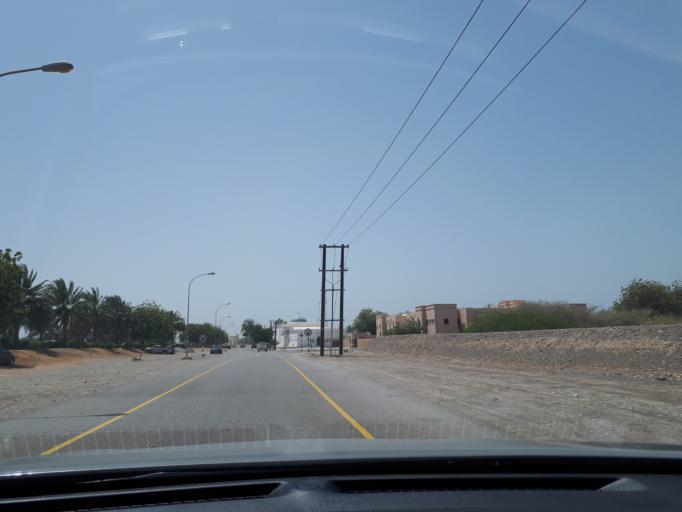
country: OM
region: Muhafazat Masqat
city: As Sib al Jadidah
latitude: 23.6923
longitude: 58.0759
